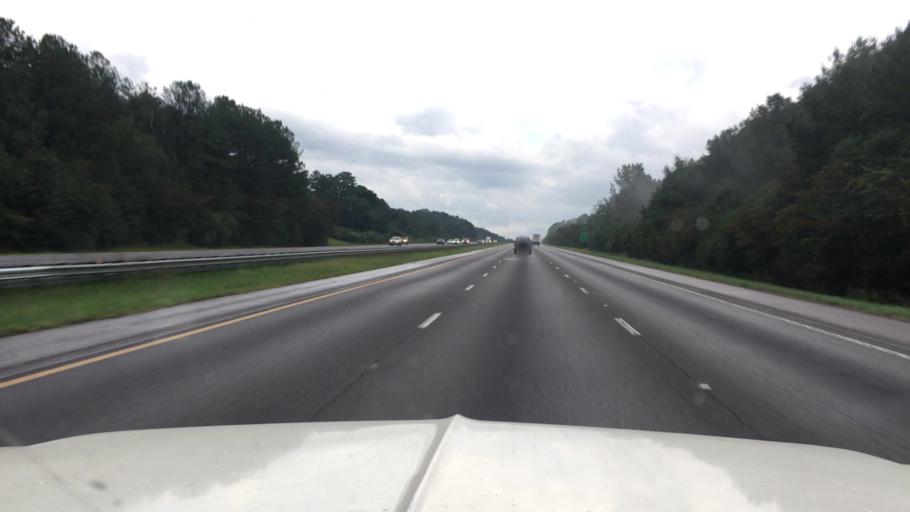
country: US
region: Alabama
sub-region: Jefferson County
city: Mount Olive
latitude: 33.6934
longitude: -86.8329
